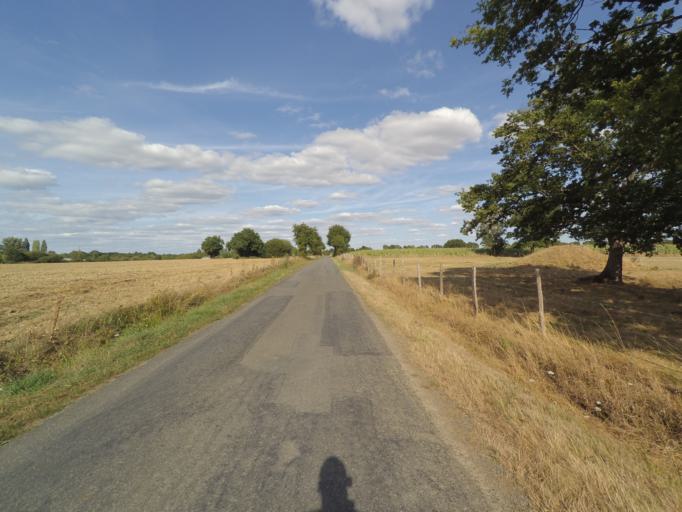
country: FR
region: Pays de la Loire
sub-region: Departement de la Loire-Atlantique
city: Vieillevigne
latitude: 46.9598
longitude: -1.4281
